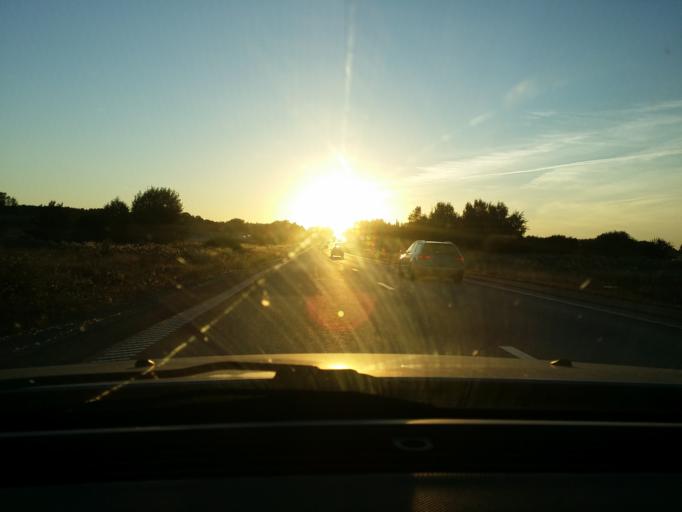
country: SE
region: Uppsala
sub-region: Enkopings Kommun
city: Grillby
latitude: 59.6346
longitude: 17.2847
